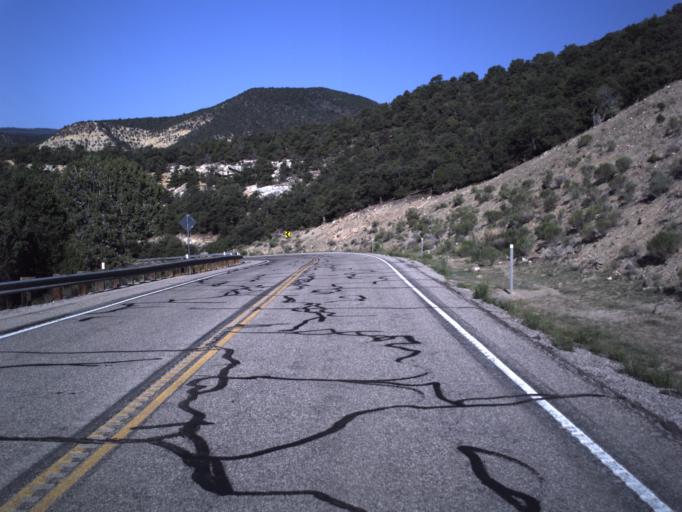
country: US
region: Utah
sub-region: Wayne County
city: Loa
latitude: 38.6757
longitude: -111.4035
